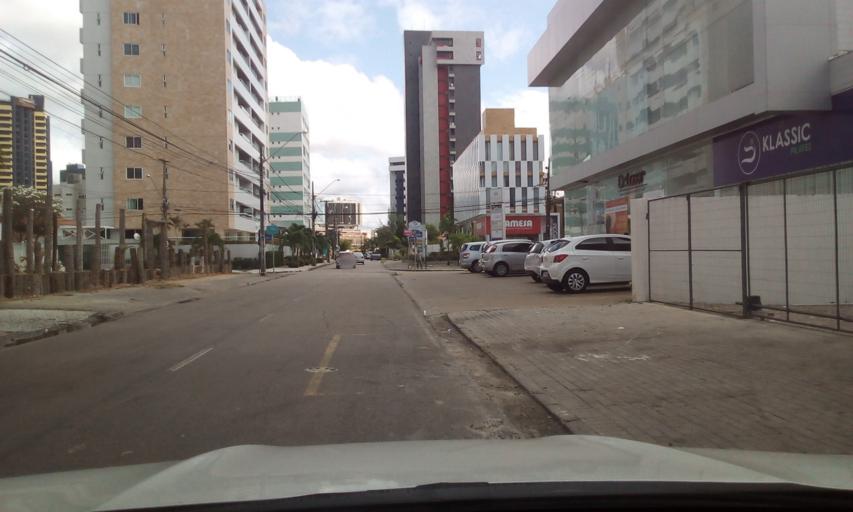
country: BR
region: Paraiba
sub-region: Joao Pessoa
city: Joao Pessoa
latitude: -7.1004
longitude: -34.8349
